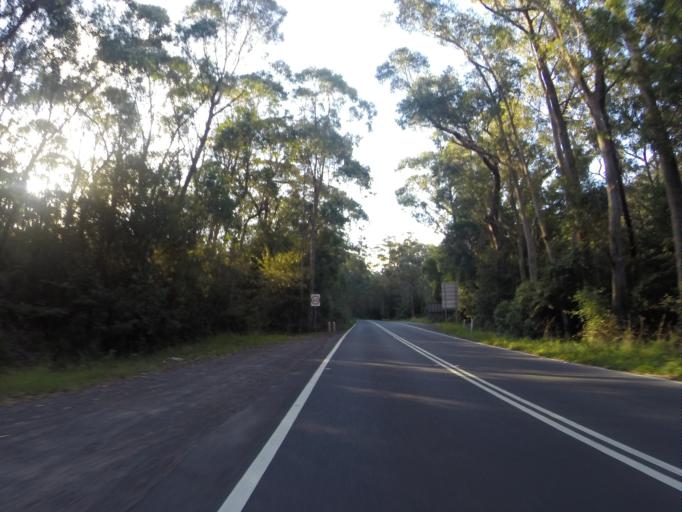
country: AU
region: New South Wales
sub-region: Shoalhaven Shire
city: Kangaroo Valley
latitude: -34.6859
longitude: 150.4911
